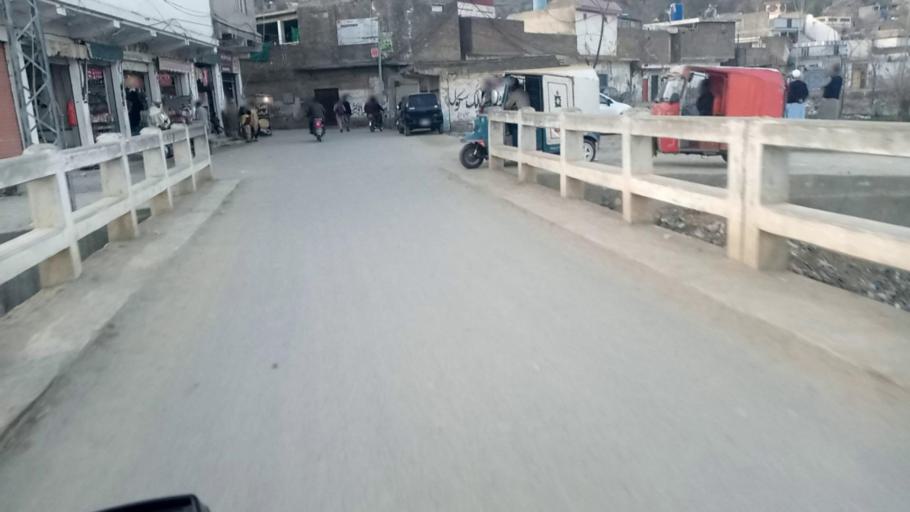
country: PK
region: Khyber Pakhtunkhwa
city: Saidu Sharif
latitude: 34.7477
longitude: 72.3499
